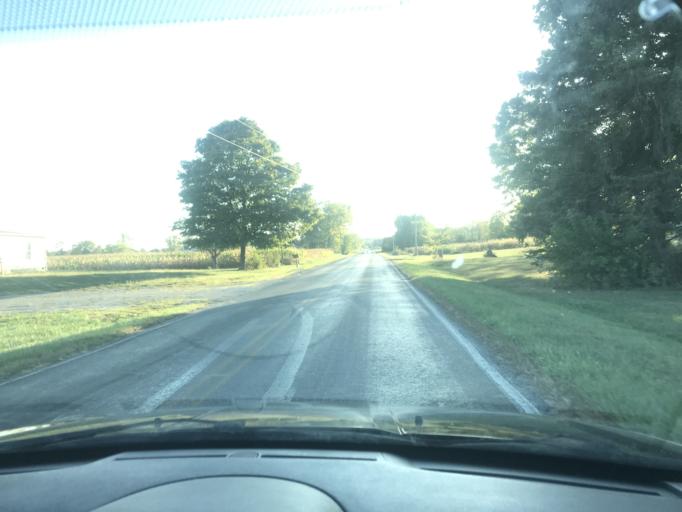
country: US
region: Ohio
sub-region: Logan County
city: De Graff
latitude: 40.2641
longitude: -83.8592
